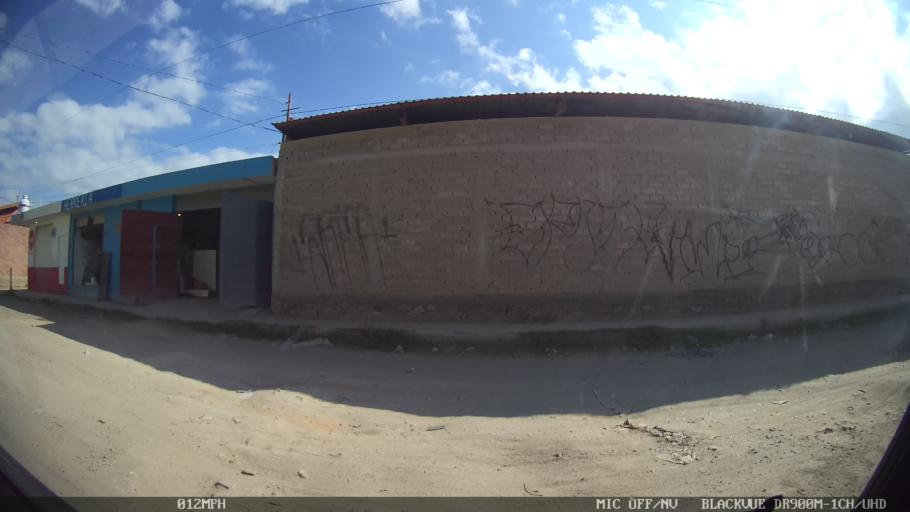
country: MX
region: Jalisco
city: Tonala
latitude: 20.6548
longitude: -103.2438
